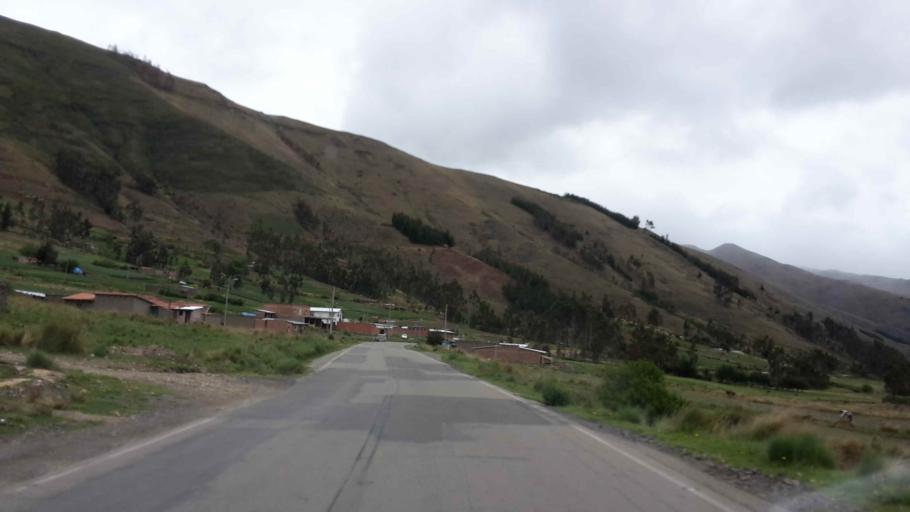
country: BO
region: Cochabamba
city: Arani
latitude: -17.4824
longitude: -65.5464
